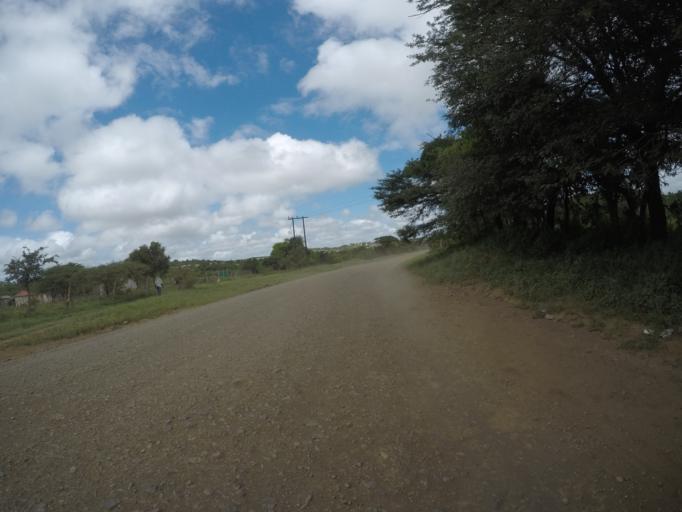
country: ZA
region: KwaZulu-Natal
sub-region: uThungulu District Municipality
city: Empangeni
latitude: -28.5874
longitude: 31.8448
